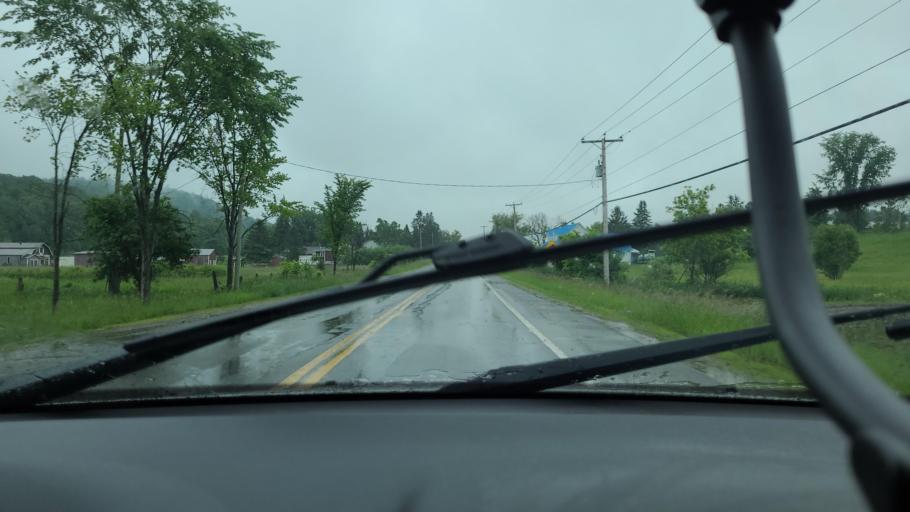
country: CA
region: Quebec
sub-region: Outaouais
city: Saint-Andre-Avellin
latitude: 45.7061
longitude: -75.0525
